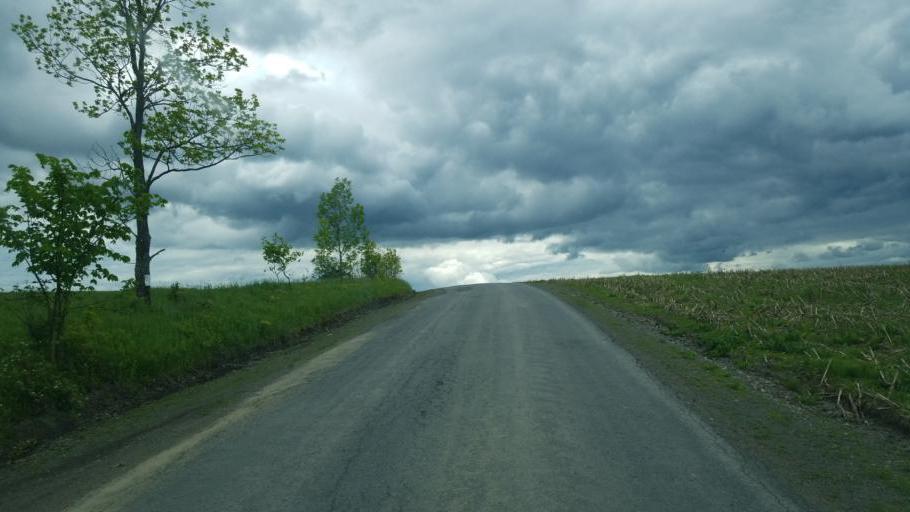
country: US
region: New York
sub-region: Otsego County
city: Richfield Springs
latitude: 42.8422
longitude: -75.1681
